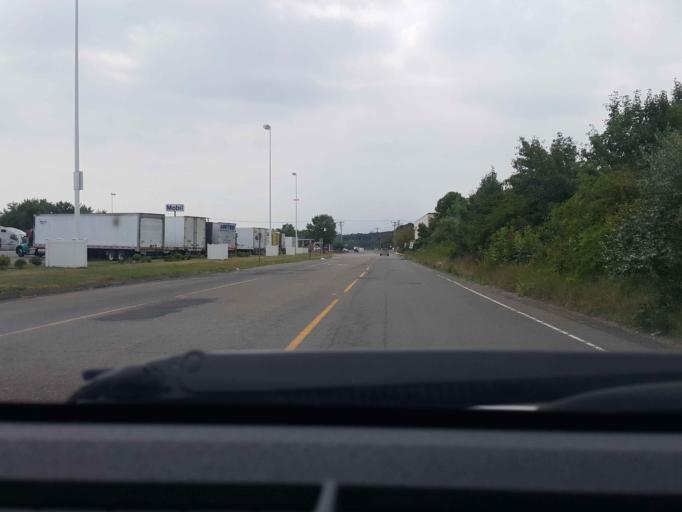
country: US
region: Connecticut
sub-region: New Haven County
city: North Branford
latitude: 41.2975
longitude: -72.7606
